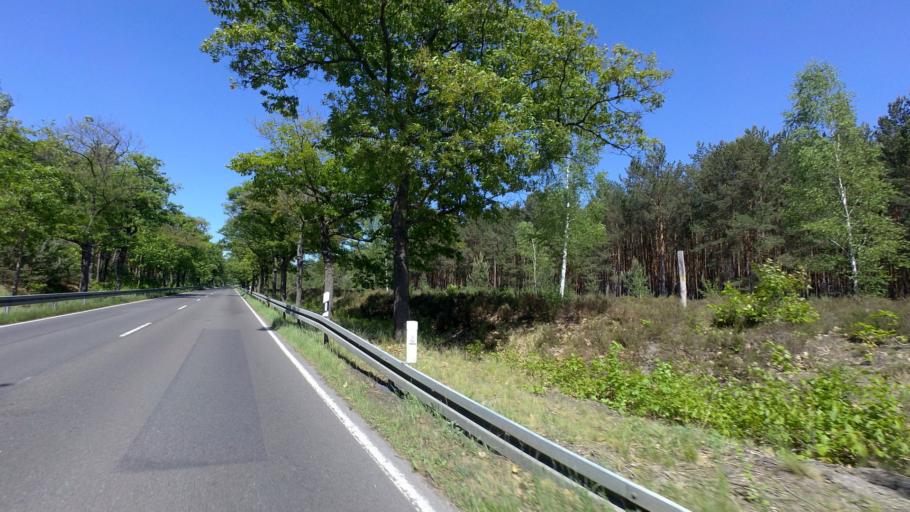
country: DE
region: Brandenburg
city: Drachhausen
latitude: 51.9111
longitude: 14.3523
